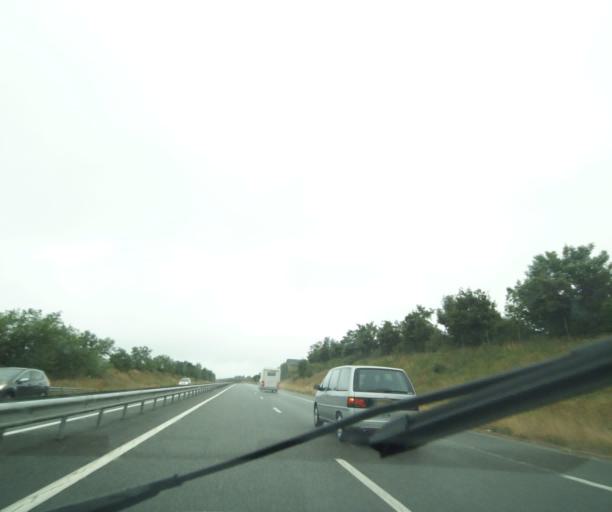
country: FR
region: Midi-Pyrenees
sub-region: Departement de l'Aveyron
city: Naucelle
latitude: 44.1088
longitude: 2.3114
